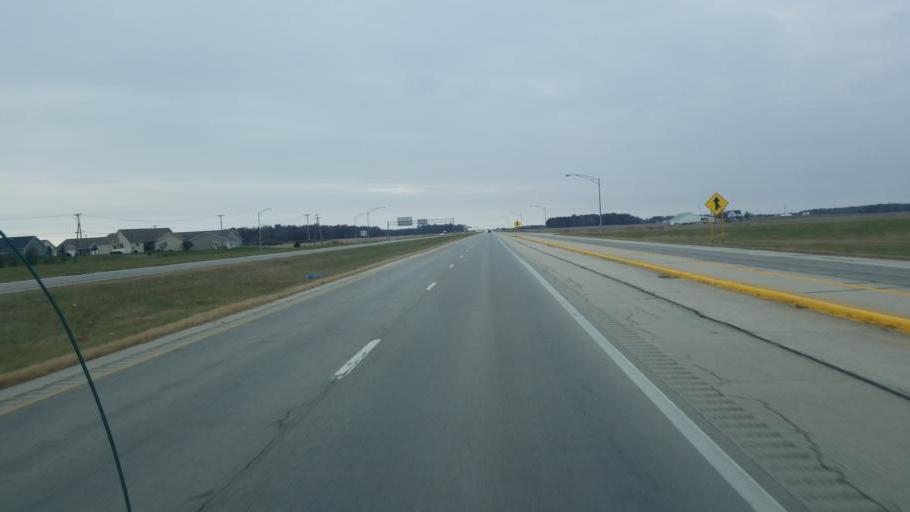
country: US
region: Ohio
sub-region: Auglaize County
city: Saint Marys
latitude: 40.5575
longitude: -84.4173
